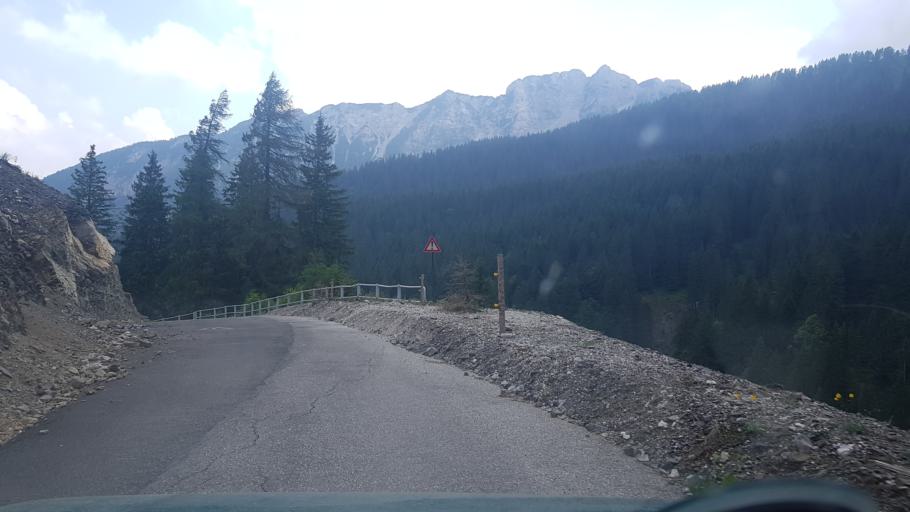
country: IT
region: Friuli Venezia Giulia
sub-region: Provincia di Udine
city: Paularo
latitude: 46.5531
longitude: 13.1912
